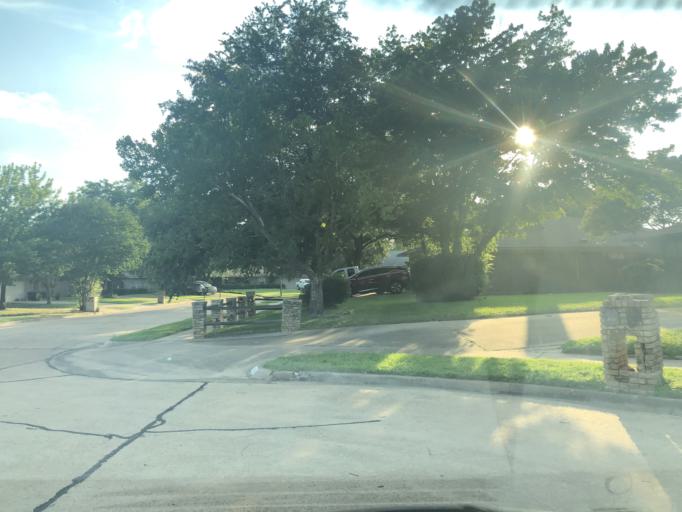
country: US
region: Texas
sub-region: Dallas County
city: Irving
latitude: 32.7964
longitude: -96.9529
